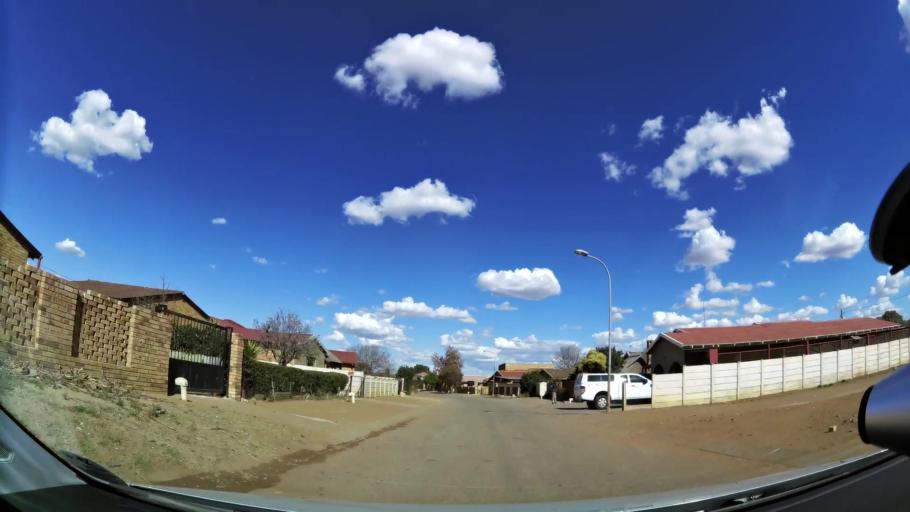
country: ZA
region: North-West
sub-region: Dr Kenneth Kaunda District Municipality
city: Klerksdorp
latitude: -26.8706
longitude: 26.5816
